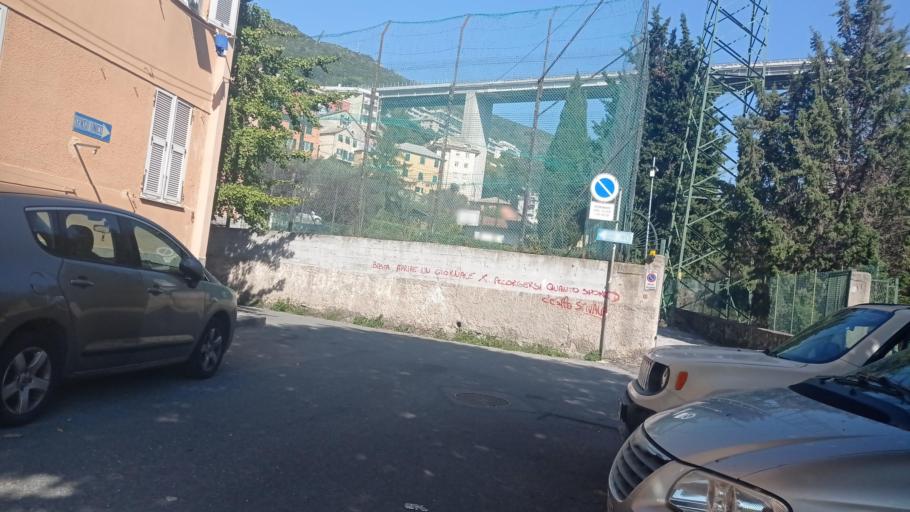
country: IT
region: Liguria
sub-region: Provincia di Genova
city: Genoa
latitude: 44.4097
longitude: 8.9896
